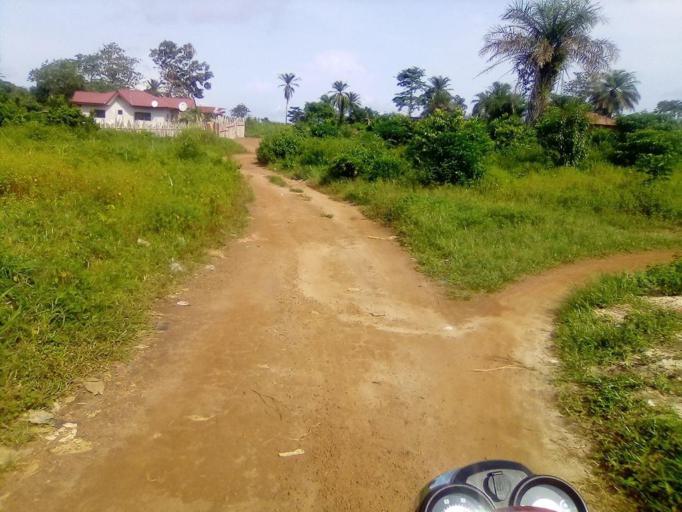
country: SL
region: Southern Province
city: Pujehun
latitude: 7.3620
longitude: -11.7268
